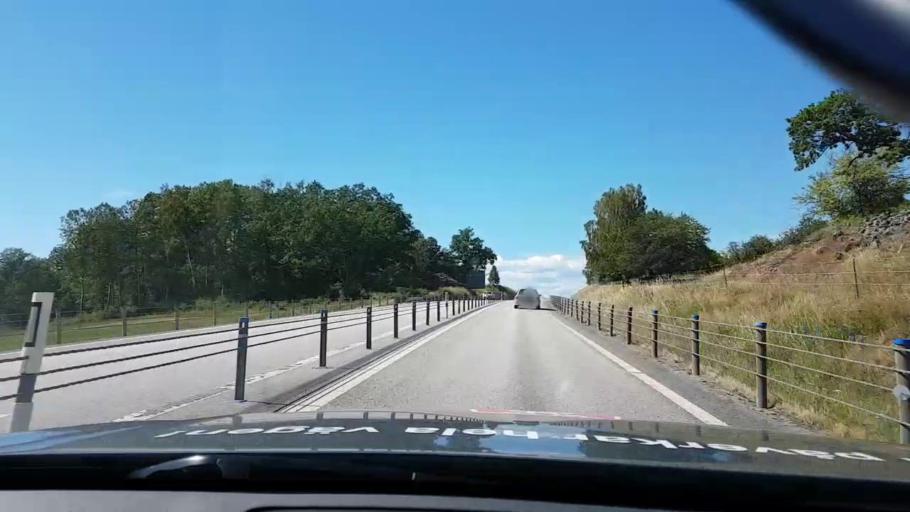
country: SE
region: Kalmar
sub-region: Vasterviks Kommun
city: Gamleby
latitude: 57.8727
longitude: 16.4069
